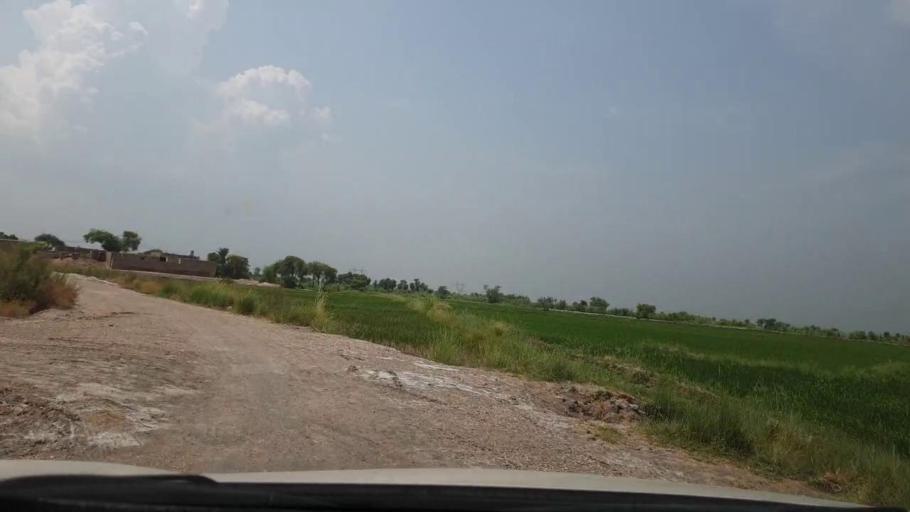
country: PK
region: Sindh
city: New Badah
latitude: 27.3897
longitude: 68.0421
